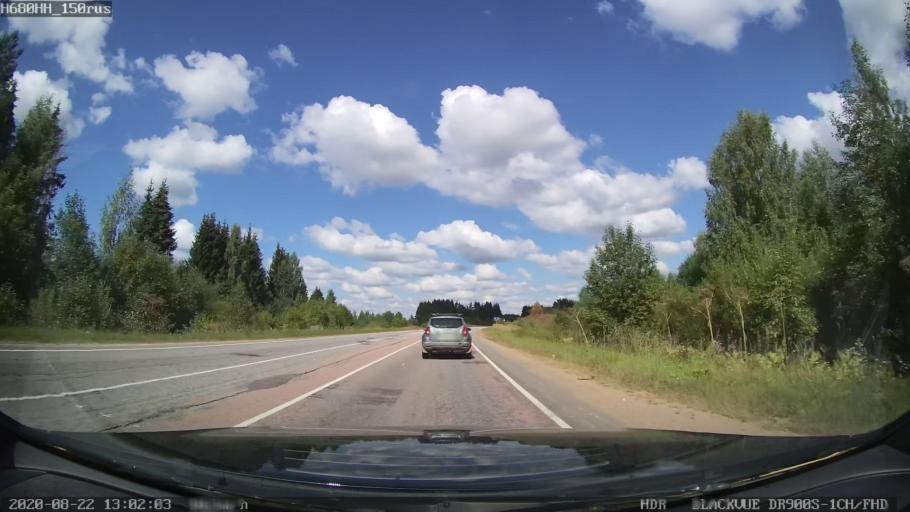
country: RU
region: Tverskaya
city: Bezhetsk
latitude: 57.6441
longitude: 36.3947
